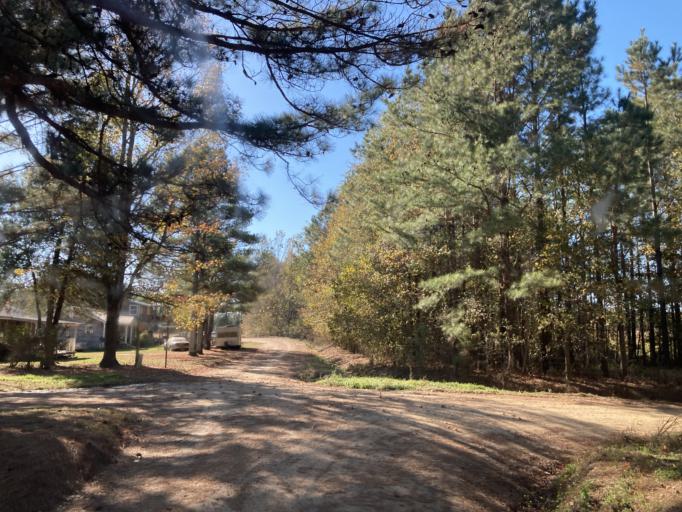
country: US
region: Mississippi
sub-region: Madison County
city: Kearney Park
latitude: 32.6718
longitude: -90.3406
